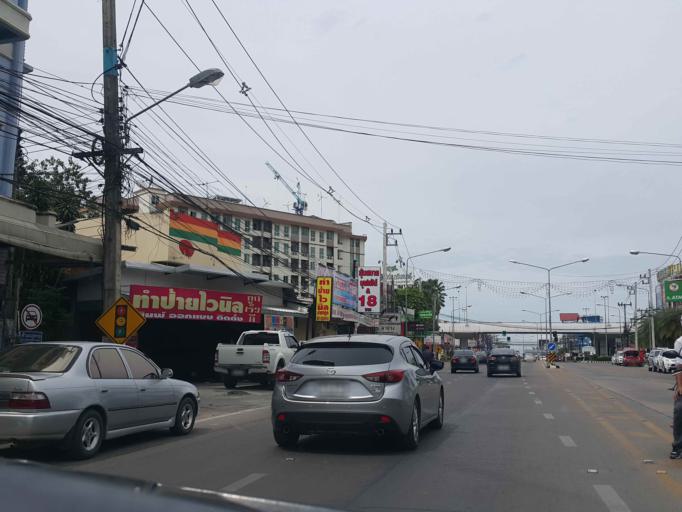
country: TH
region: Chiang Mai
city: Chiang Mai
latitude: 18.7704
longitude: 98.9784
